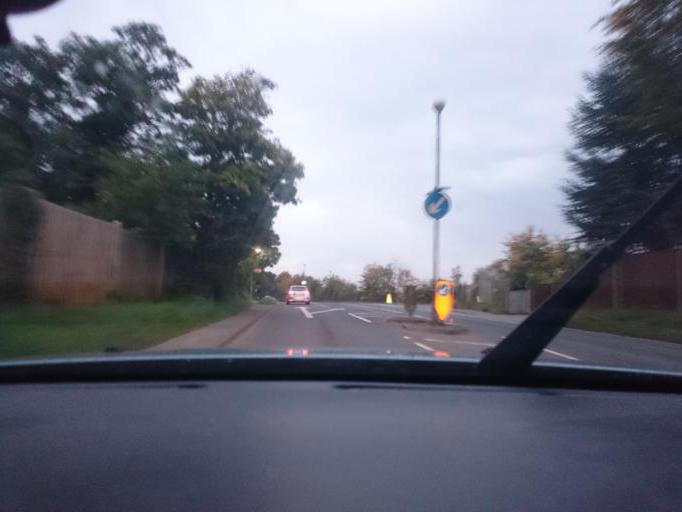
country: GB
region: England
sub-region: Hampshire
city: Aldershot
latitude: 51.2208
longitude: -0.7560
